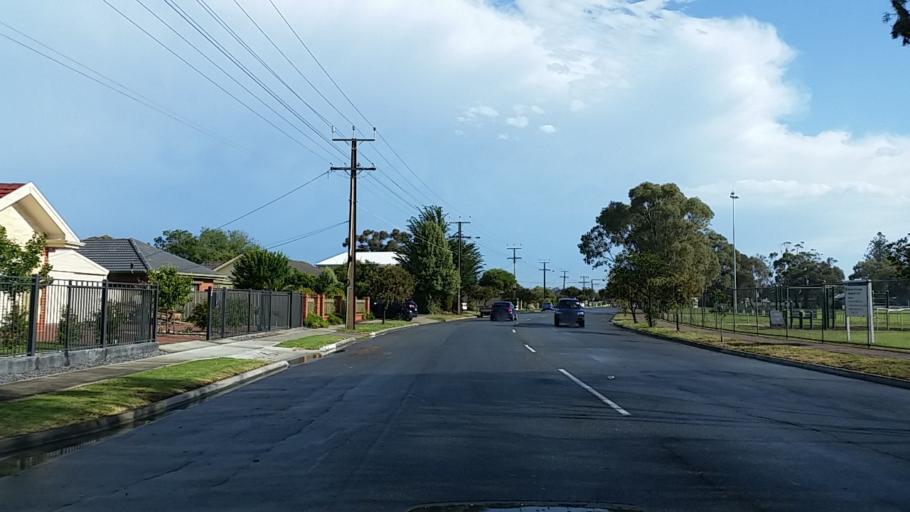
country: AU
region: South Australia
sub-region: Charles Sturt
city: Henley Beach
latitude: -34.9182
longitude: 138.5012
